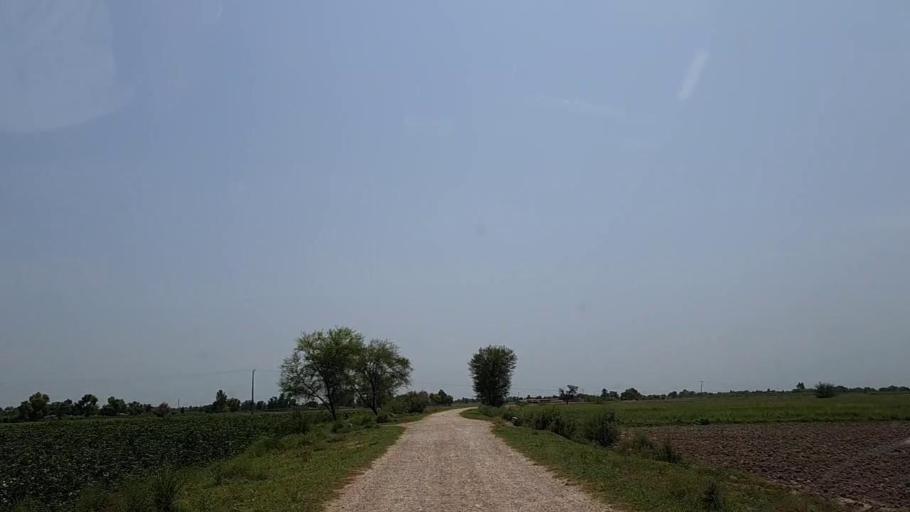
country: PK
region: Sindh
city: Ghotki
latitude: 27.9922
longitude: 69.4102
